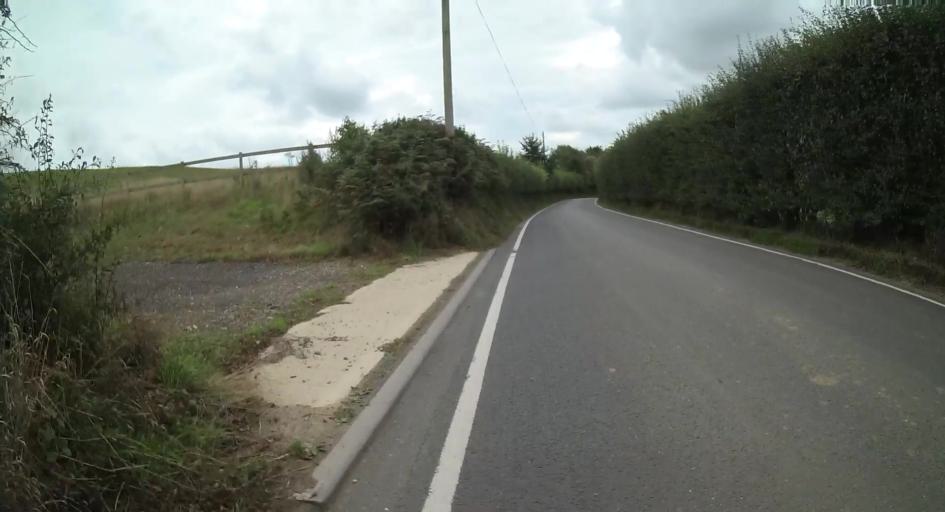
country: GB
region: England
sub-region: Isle of Wight
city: Niton
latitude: 50.6110
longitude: -1.2677
